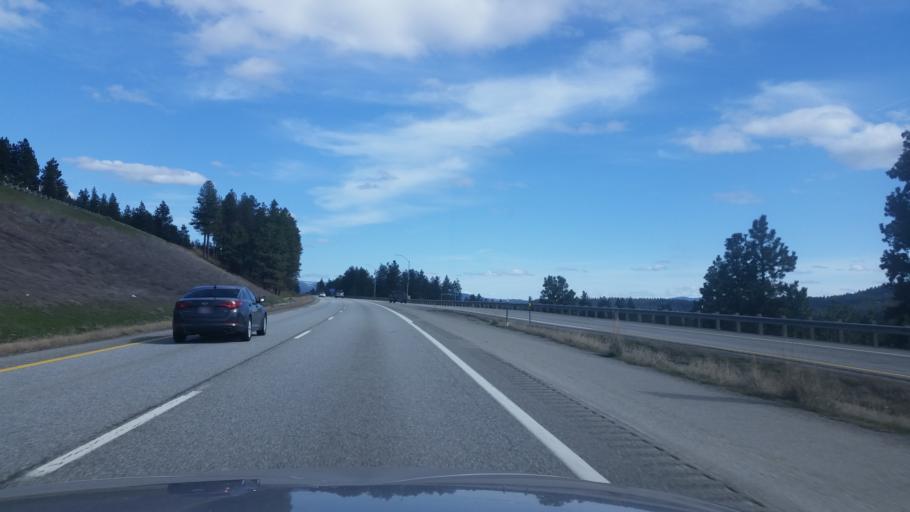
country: US
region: Idaho
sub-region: Kootenai County
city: Post Falls
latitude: 47.7090
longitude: -116.8888
